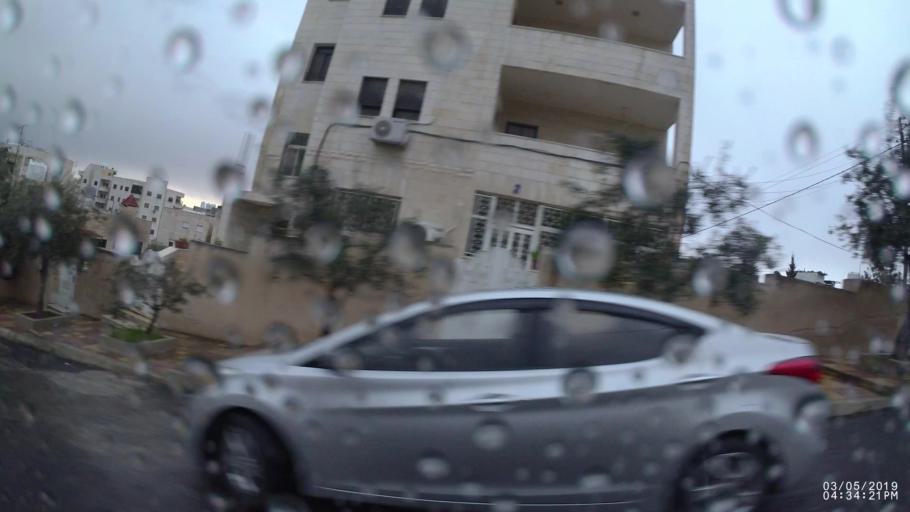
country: JO
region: Amman
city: Amman
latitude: 31.9995
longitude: 35.9661
